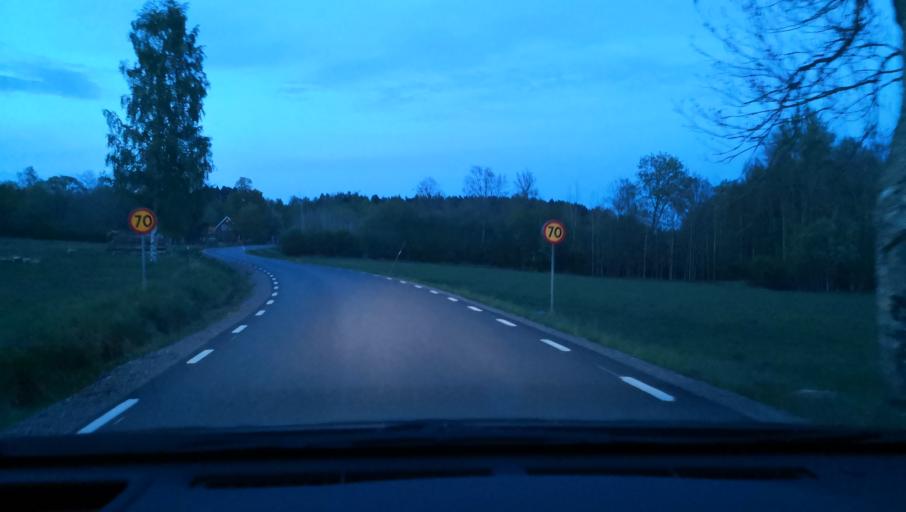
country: SE
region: OErebro
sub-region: Askersunds Kommun
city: Asbro
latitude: 59.0681
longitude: 14.9765
